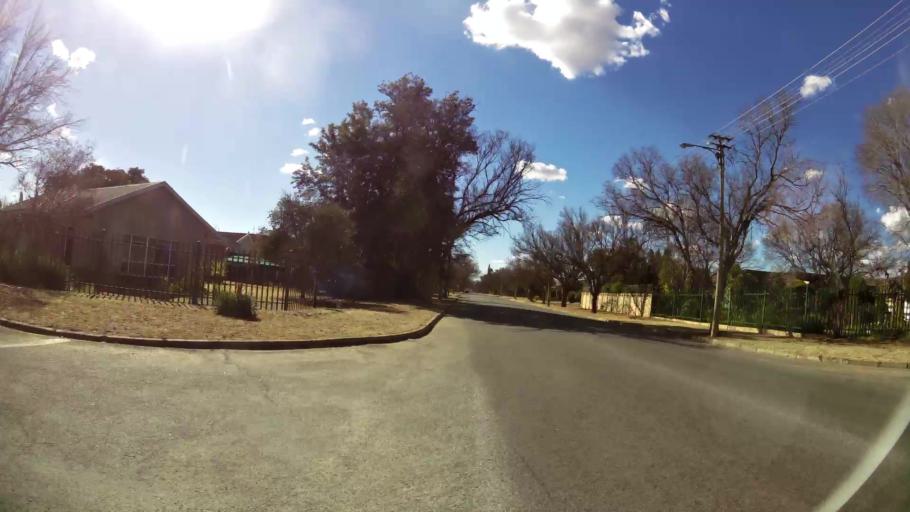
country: ZA
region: North-West
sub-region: Dr Kenneth Kaunda District Municipality
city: Klerksdorp
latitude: -26.8590
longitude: 26.6401
